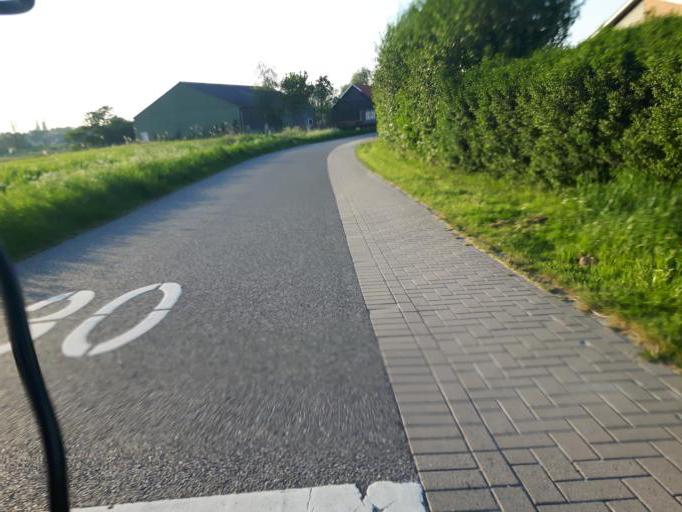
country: NL
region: Zeeland
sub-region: Gemeente Goes
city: Goes
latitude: 51.4989
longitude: 3.8614
